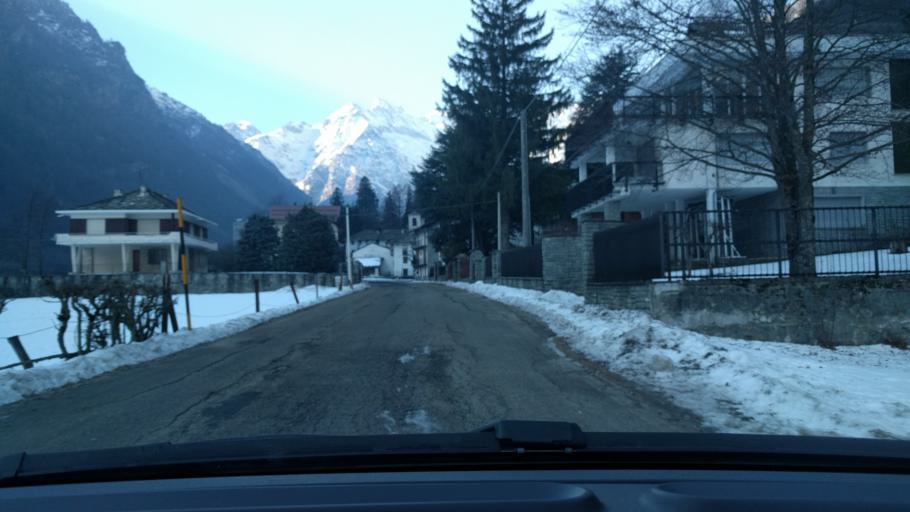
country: IT
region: Piedmont
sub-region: Provincia di Torino
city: Groscavallo
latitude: 45.3699
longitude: 7.2735
